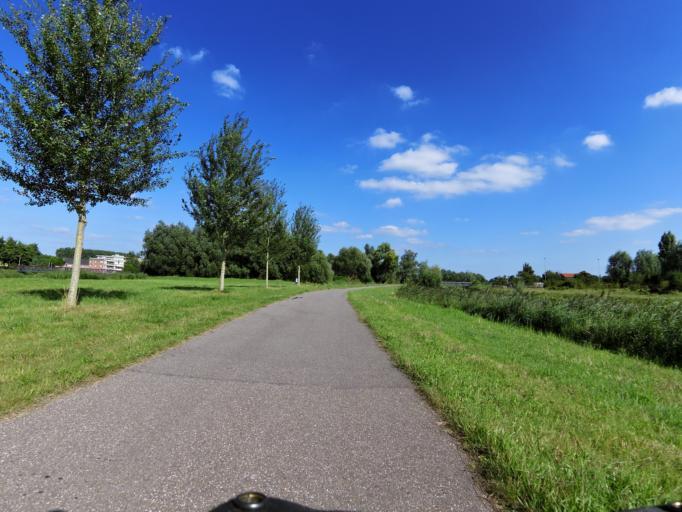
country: NL
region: South Holland
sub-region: Gemeente Binnenmaas
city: Heinenoord
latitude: 51.8511
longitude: 4.4759
